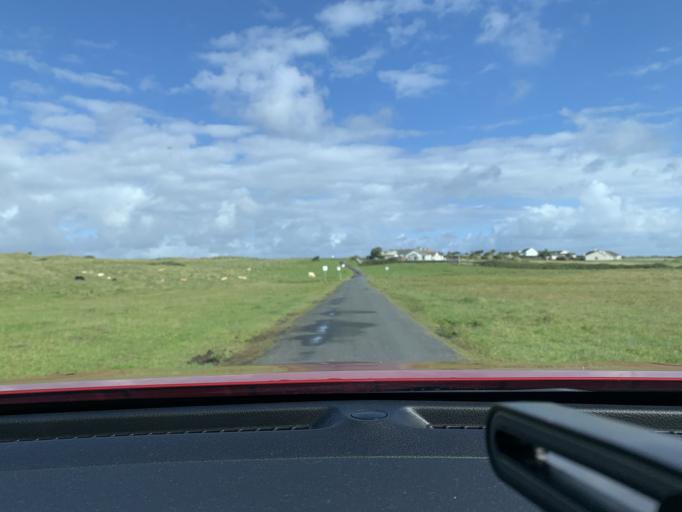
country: IE
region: Connaught
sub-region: Sligo
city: Strandhill
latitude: 54.4004
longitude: -8.5644
